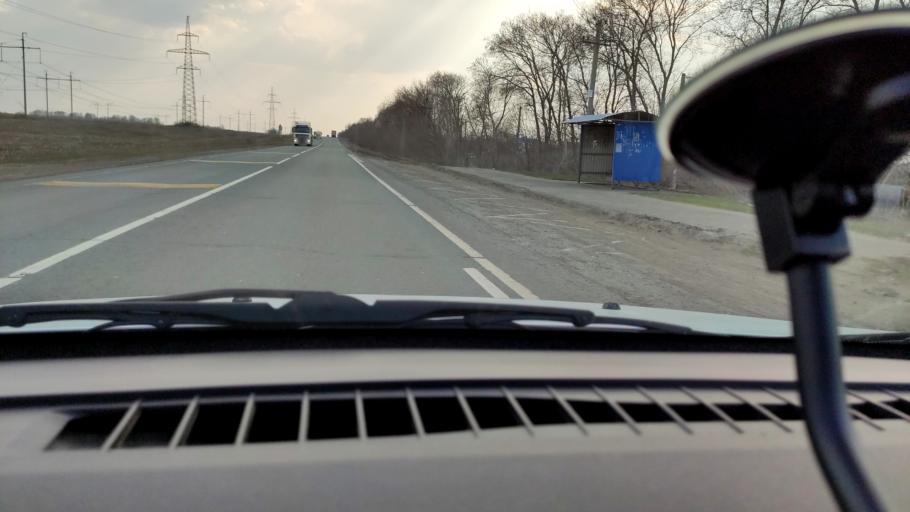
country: RU
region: Samara
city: Dubovyy Umet
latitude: 53.0819
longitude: 50.3905
